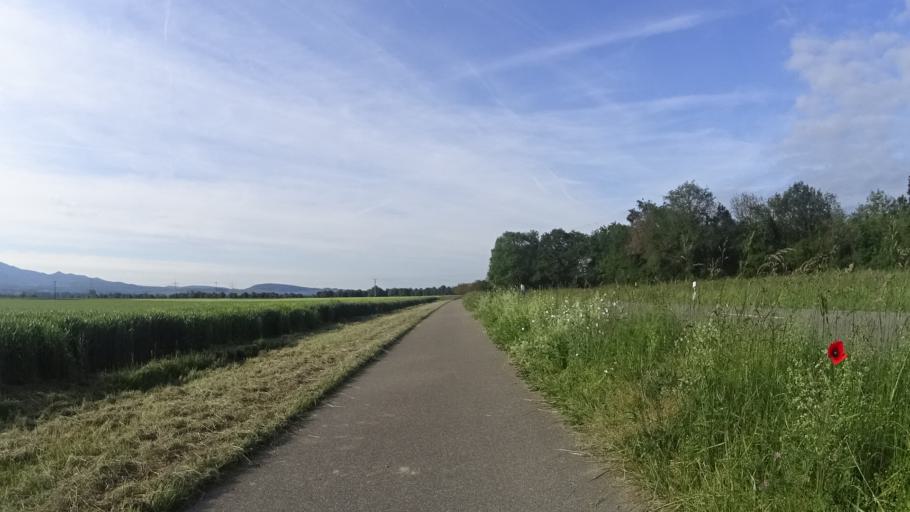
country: DE
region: Baden-Wuerttemberg
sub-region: Freiburg Region
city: Neuenburg am Rhein
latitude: 47.8513
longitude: 7.5837
